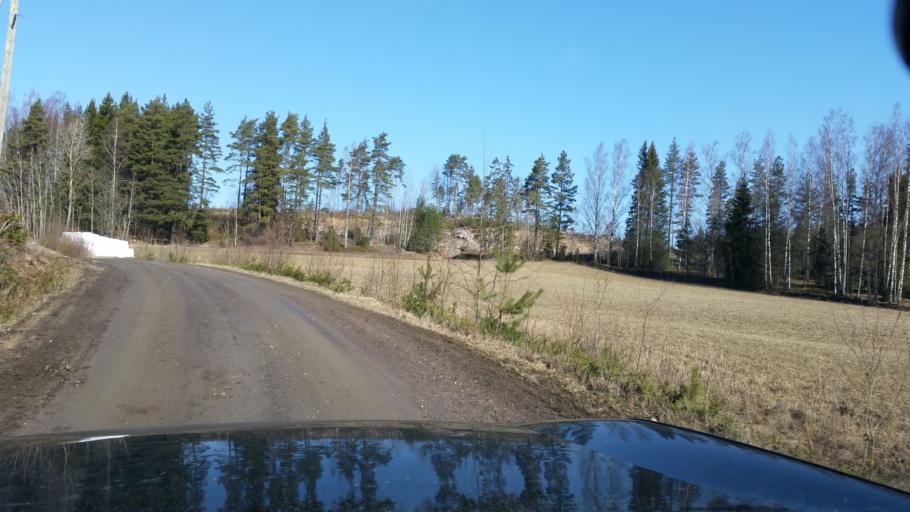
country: FI
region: Uusimaa
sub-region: Helsinki
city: Karjalohja
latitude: 60.2115
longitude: 23.7021
